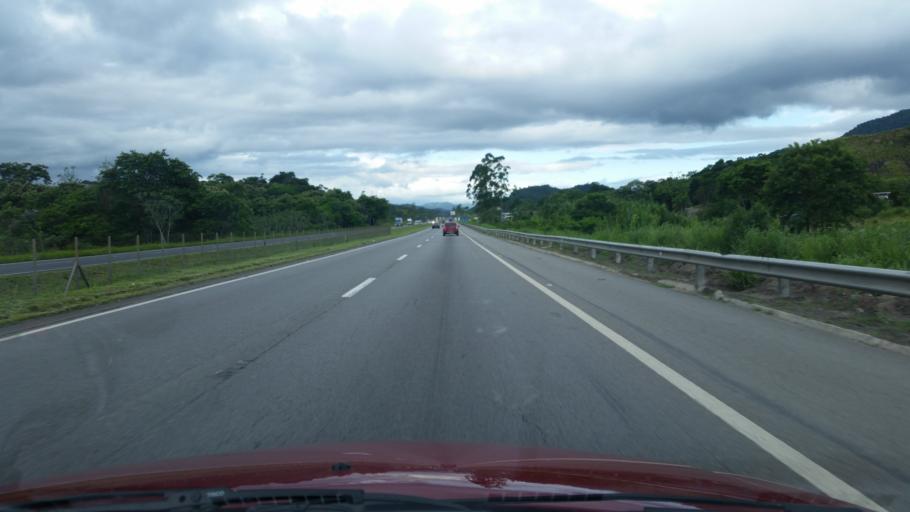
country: BR
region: Sao Paulo
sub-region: Miracatu
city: Miracatu
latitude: -24.2760
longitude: -47.4139
